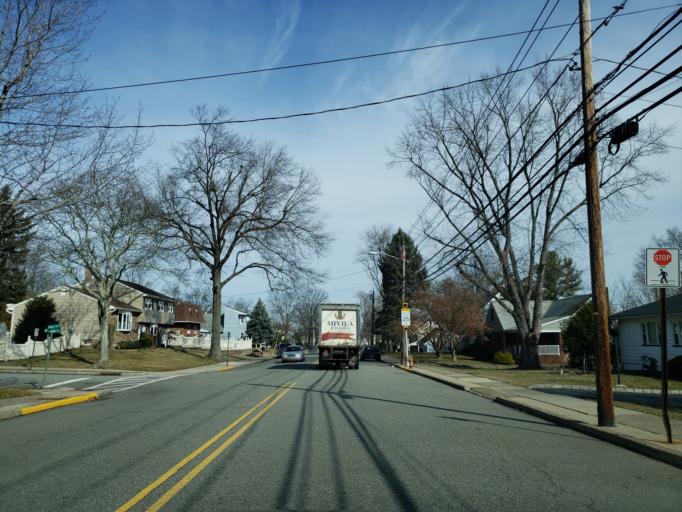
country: US
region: New Jersey
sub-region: Passaic County
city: Singac
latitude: 40.8713
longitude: -74.2339
